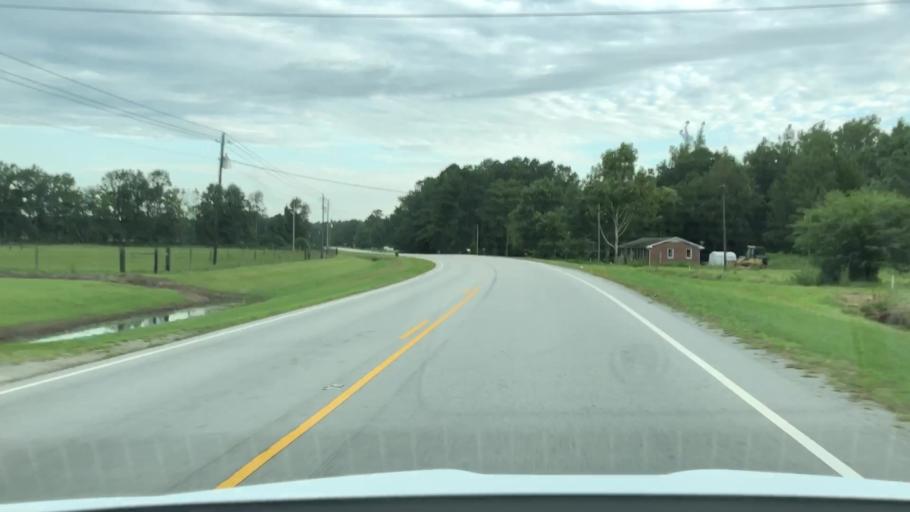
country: US
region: North Carolina
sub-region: Jones County
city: Trenton
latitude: 35.0280
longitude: -77.3096
